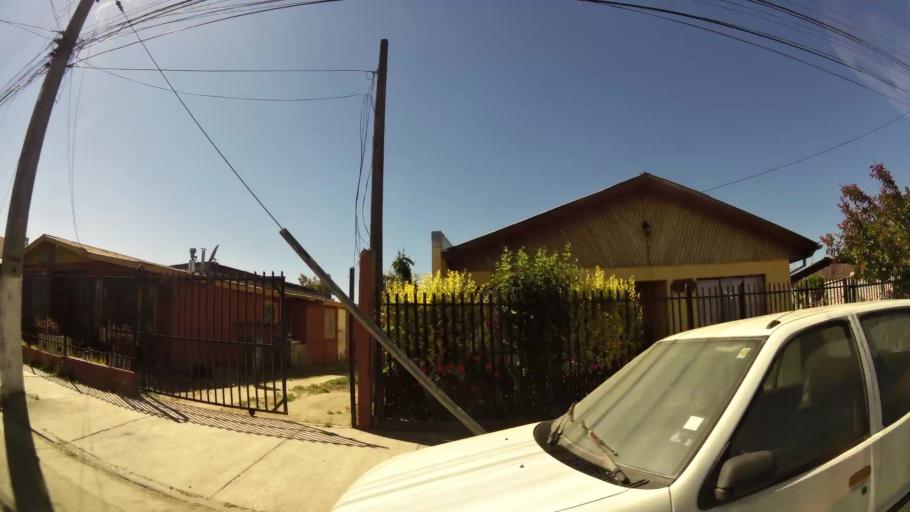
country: CL
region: Valparaiso
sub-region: Provincia de Marga Marga
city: Quilpue
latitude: -33.3138
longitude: -71.4108
